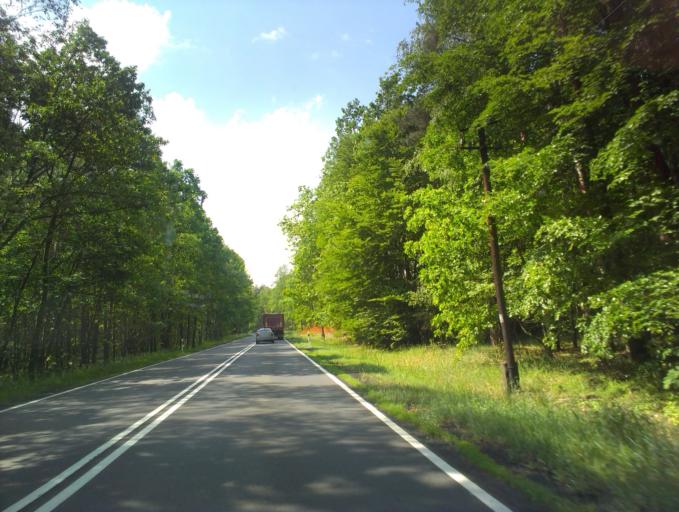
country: PL
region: Greater Poland Voivodeship
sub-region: Powiat zlotowski
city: Tarnowka
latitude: 53.2962
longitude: 16.7837
